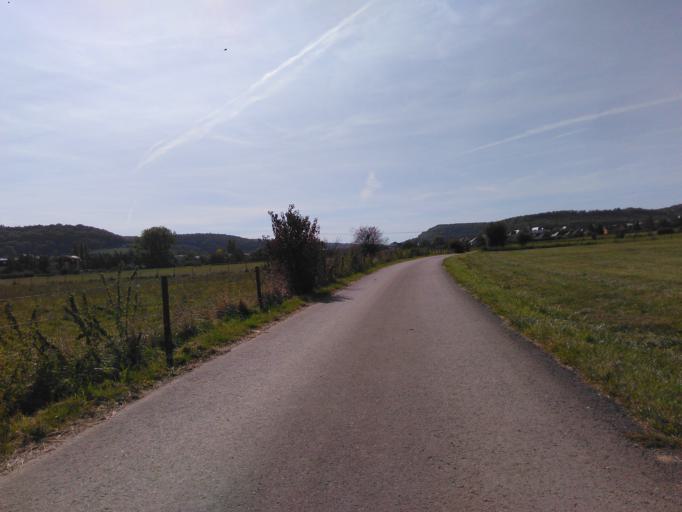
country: LU
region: Luxembourg
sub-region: Canton d'Esch-sur-Alzette
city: Kayl
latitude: 49.4968
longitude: 6.0459
